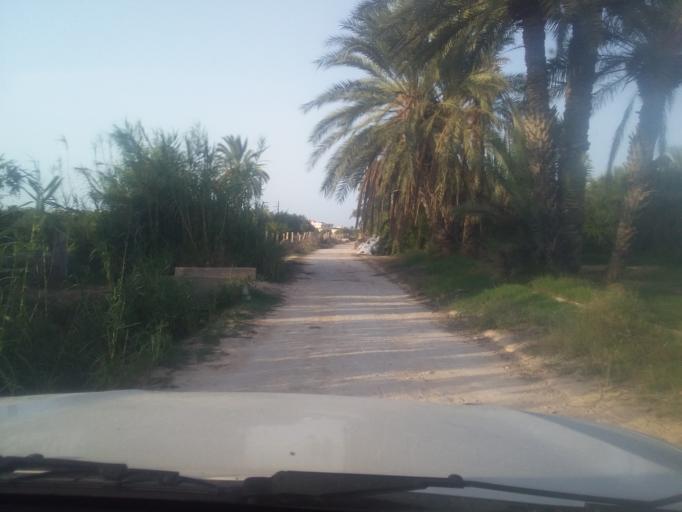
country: TN
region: Qabis
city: Gabes
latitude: 33.6305
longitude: 10.2912
